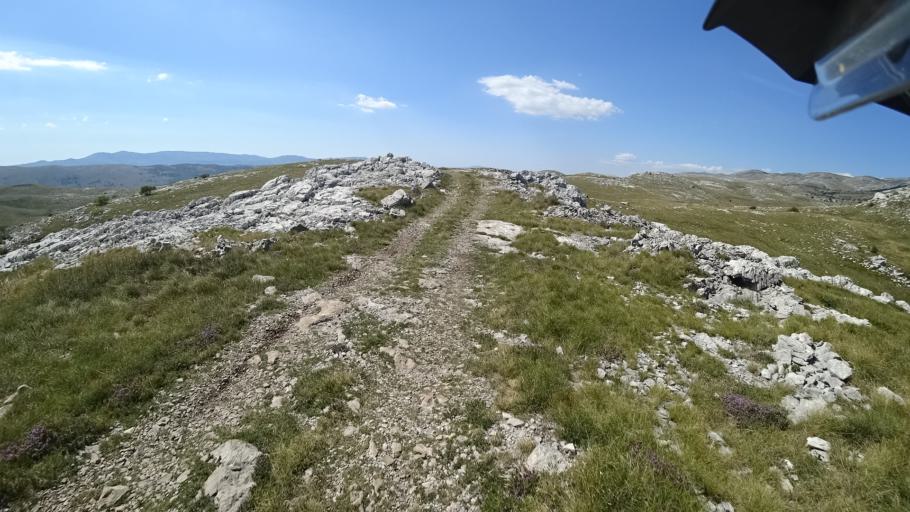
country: HR
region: Splitsko-Dalmatinska
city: Hrvace
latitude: 43.8947
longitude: 16.6300
